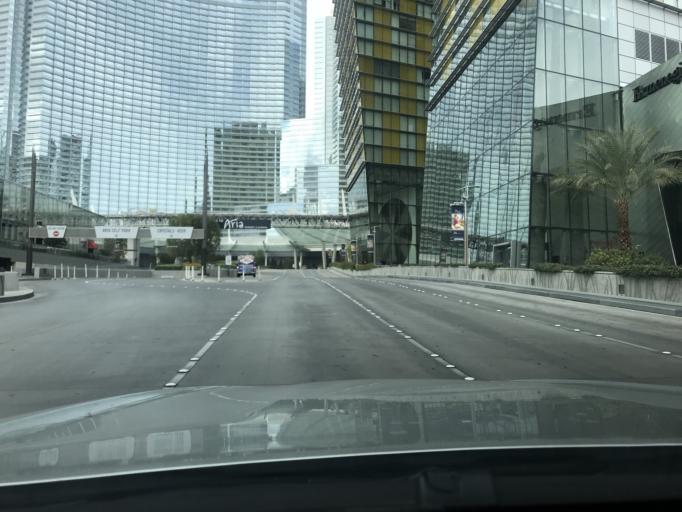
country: US
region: Nevada
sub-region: Clark County
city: Paradise
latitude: 36.1068
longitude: -115.1739
